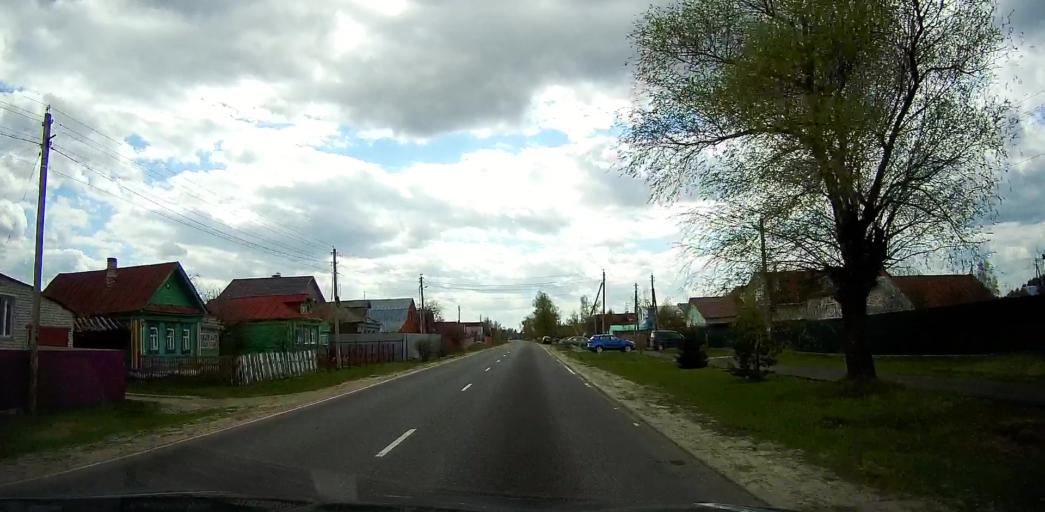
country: RU
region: Moskovskaya
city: Drezna
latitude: 55.6676
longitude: 38.7625
